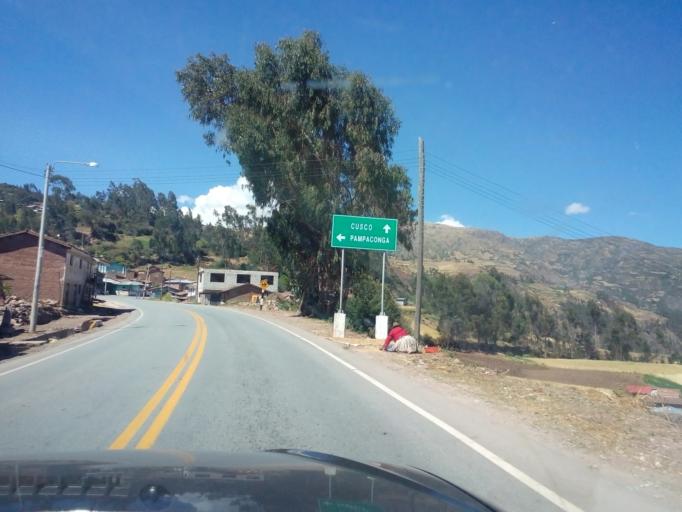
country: PE
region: Cusco
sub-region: Provincia de Anta
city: Limatambo
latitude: -13.4430
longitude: -72.4032
